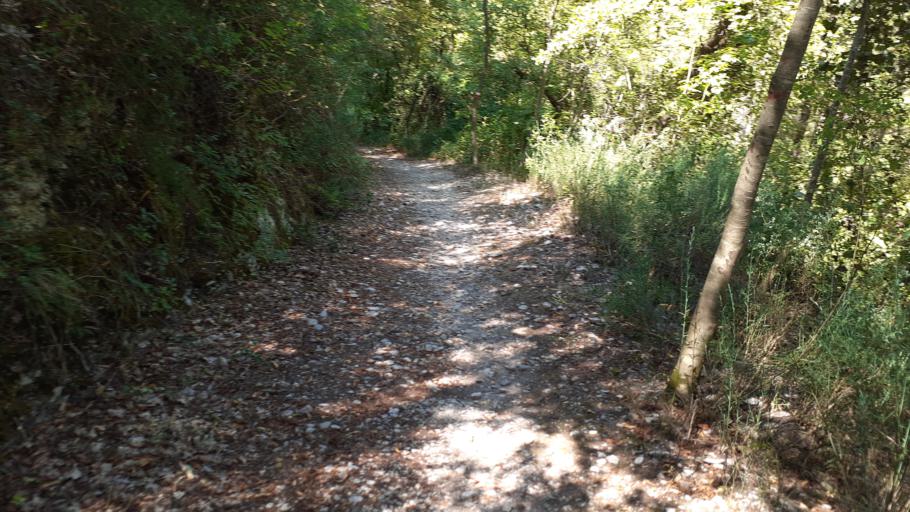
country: IT
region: Abruzzo
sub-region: Provincia di Pescara
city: San Valentino in Abruzzo Citeriore
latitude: 42.2431
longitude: 13.9698
